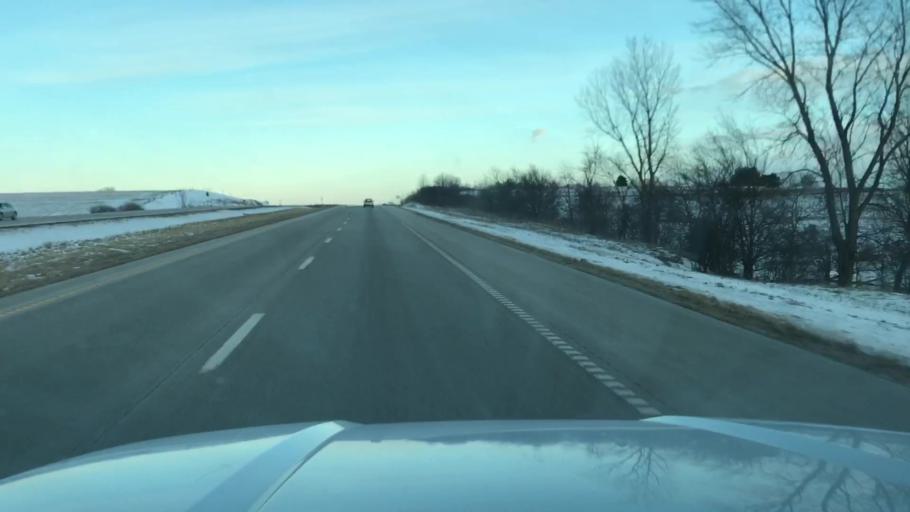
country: US
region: Missouri
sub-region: Andrew County
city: Country Club Village
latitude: 39.7475
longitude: -94.6890
